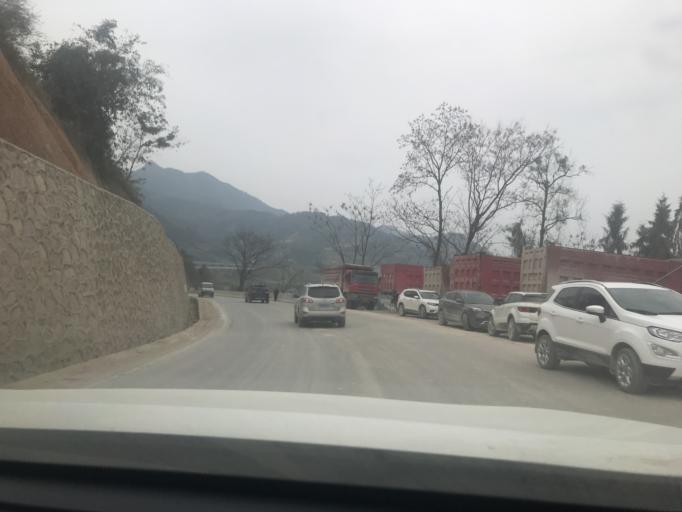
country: CN
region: Guangxi Zhuangzu Zizhiqu
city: Xinzhou
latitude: 25.0198
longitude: 105.8634
